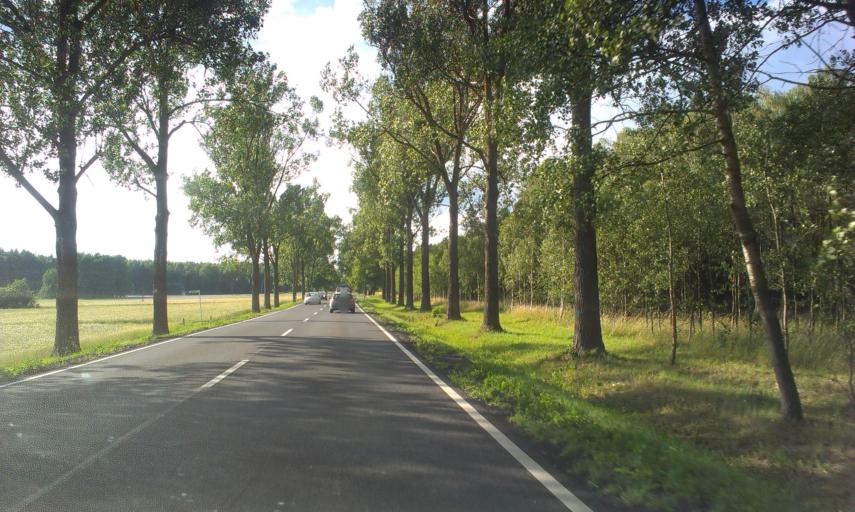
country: PL
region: Greater Poland Voivodeship
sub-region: Powiat zlotowski
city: Okonek
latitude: 53.4917
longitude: 16.8637
